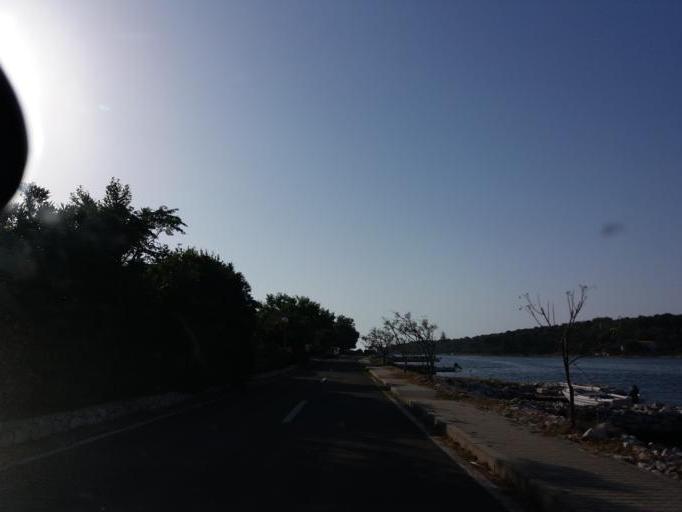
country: HR
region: Zadarska
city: Ugljan
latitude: 44.1402
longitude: 14.8543
